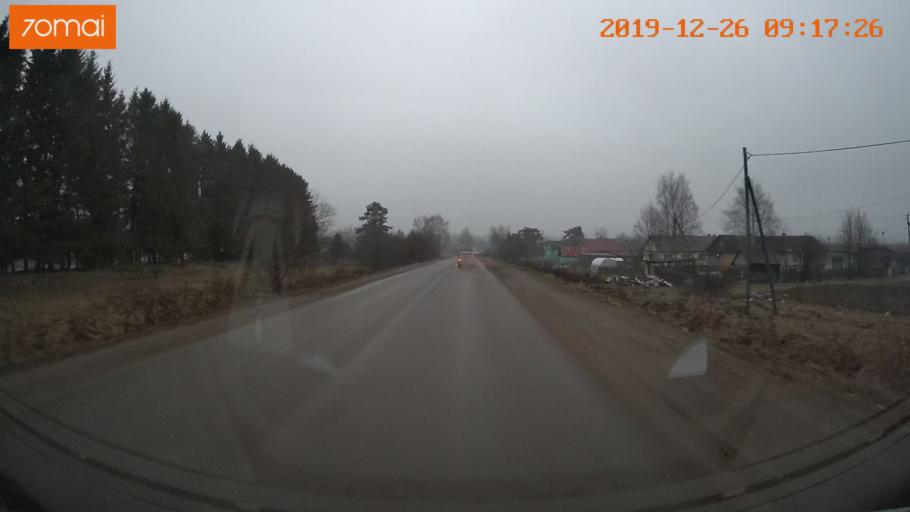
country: RU
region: Vologda
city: Gryazovets
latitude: 58.9296
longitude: 40.2392
